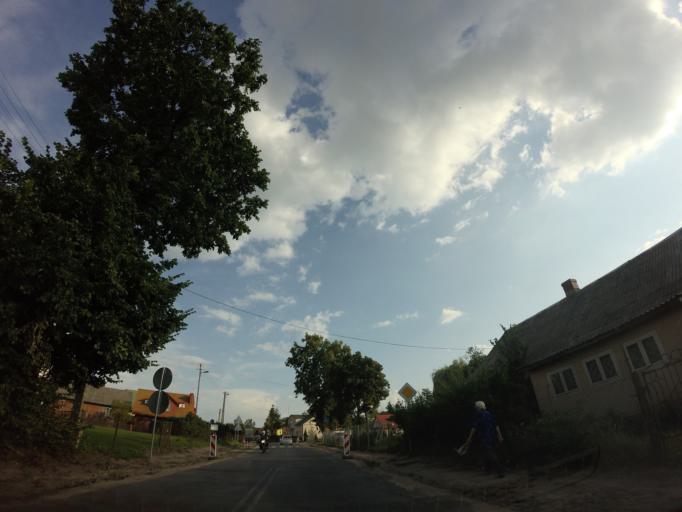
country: PL
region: Lublin Voivodeship
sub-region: Powiat lubartowski
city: Przytoczno
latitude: 51.6149
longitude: 22.2734
